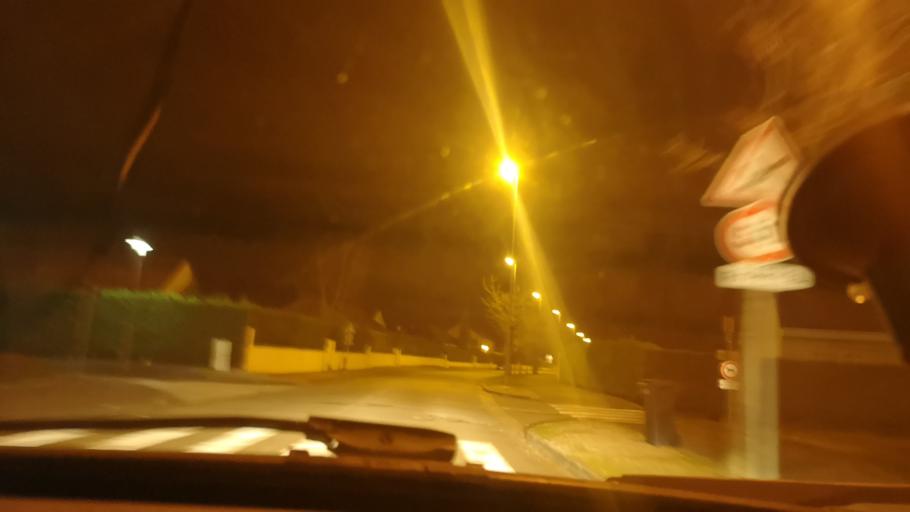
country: FR
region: Bourgogne
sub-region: Departement de Saone-et-Loire
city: Saint-Remy
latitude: 46.7650
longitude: 4.8279
